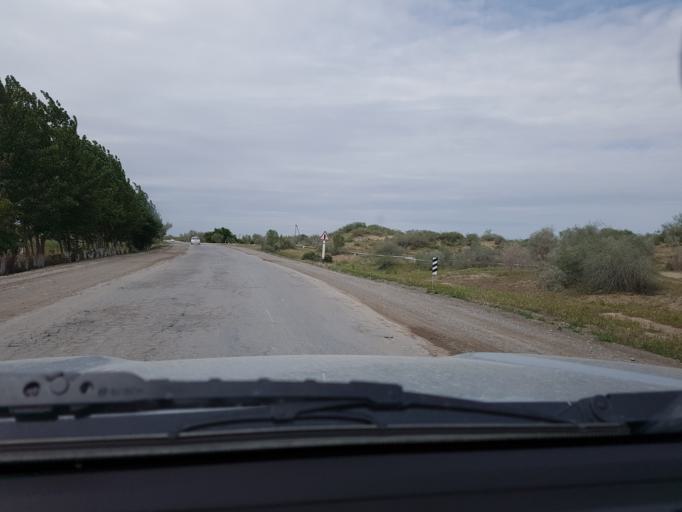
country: TM
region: Lebap
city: Atamyrat
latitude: 38.1129
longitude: 64.7352
